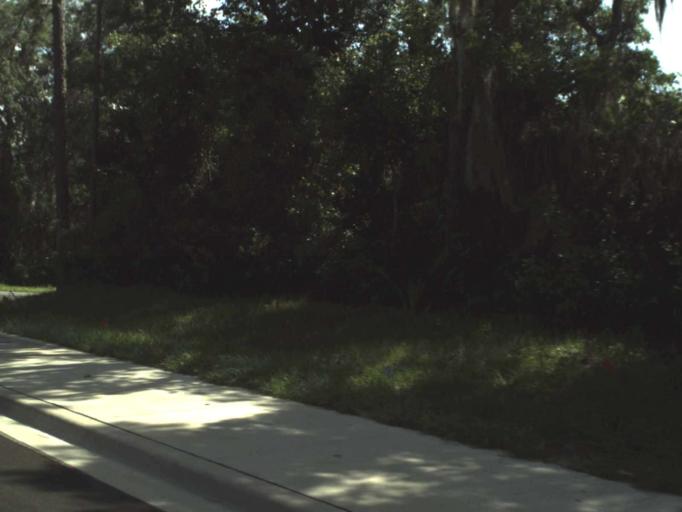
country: US
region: Florida
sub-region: Seminole County
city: Midway
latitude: 28.8692
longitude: -81.1622
